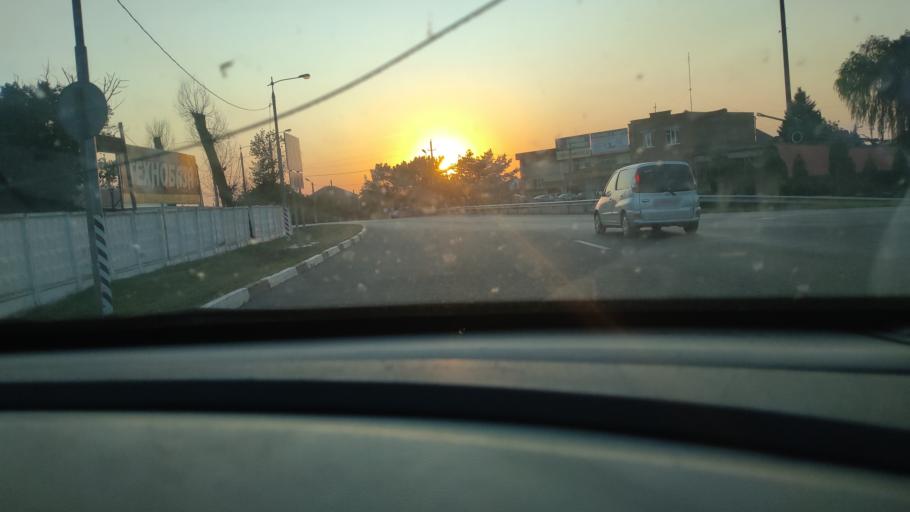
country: RU
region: Krasnodarskiy
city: Timashevsk
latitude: 45.6005
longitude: 38.9309
